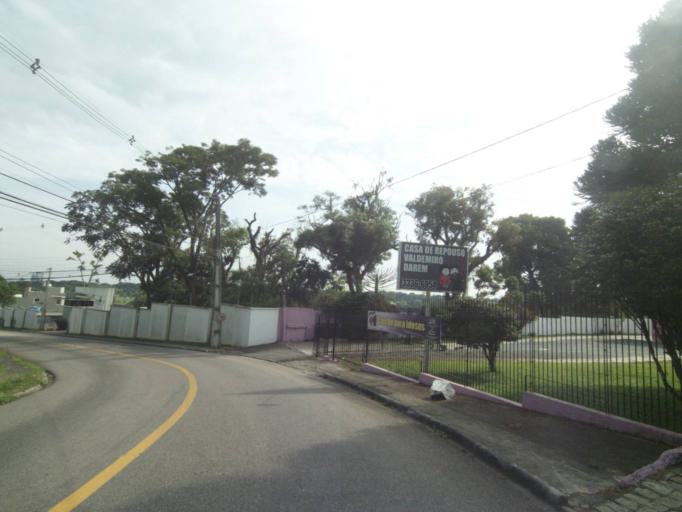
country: BR
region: Parana
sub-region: Curitiba
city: Curitiba
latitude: -25.4113
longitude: -49.3122
